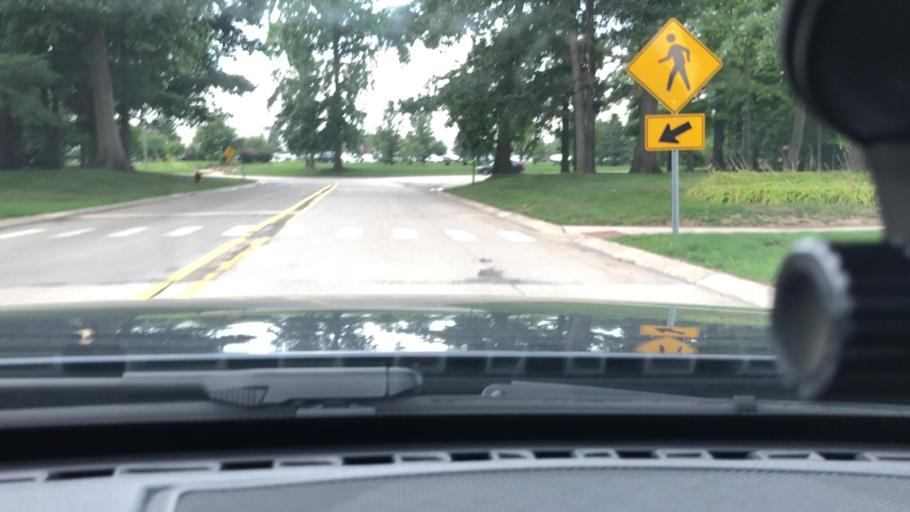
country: US
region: Michigan
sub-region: Wayne County
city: Livonia
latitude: 42.3727
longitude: -83.3398
